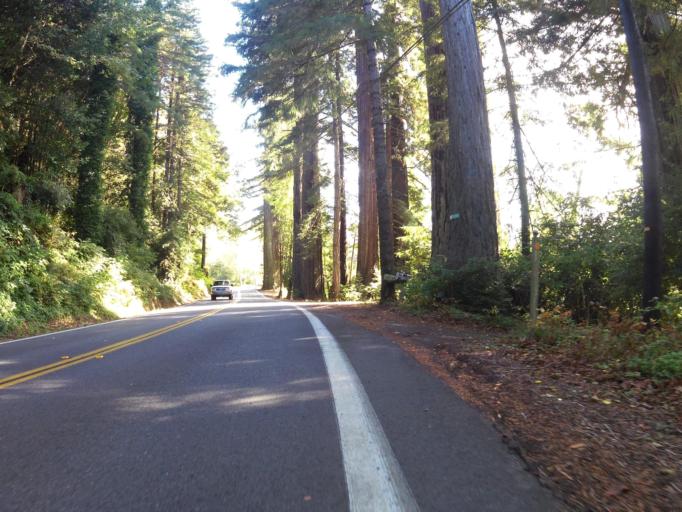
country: US
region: California
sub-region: Del Norte County
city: Bertsch-Oceanview
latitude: 41.8429
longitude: -124.1135
